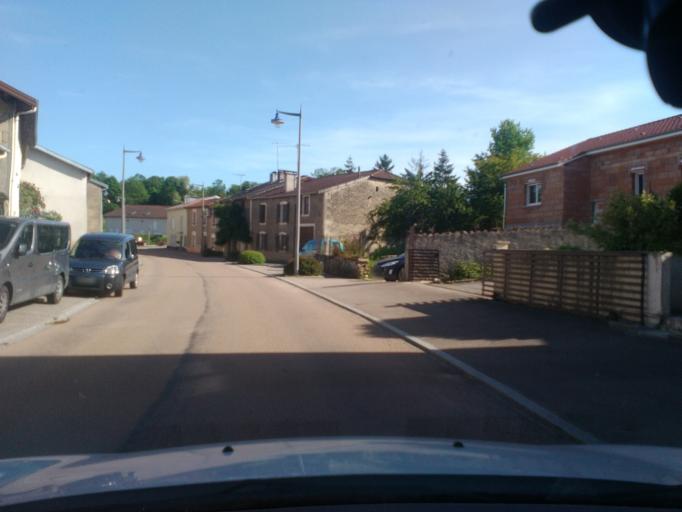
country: FR
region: Lorraine
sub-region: Departement des Vosges
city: Mirecourt
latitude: 48.2238
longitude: 6.2193
